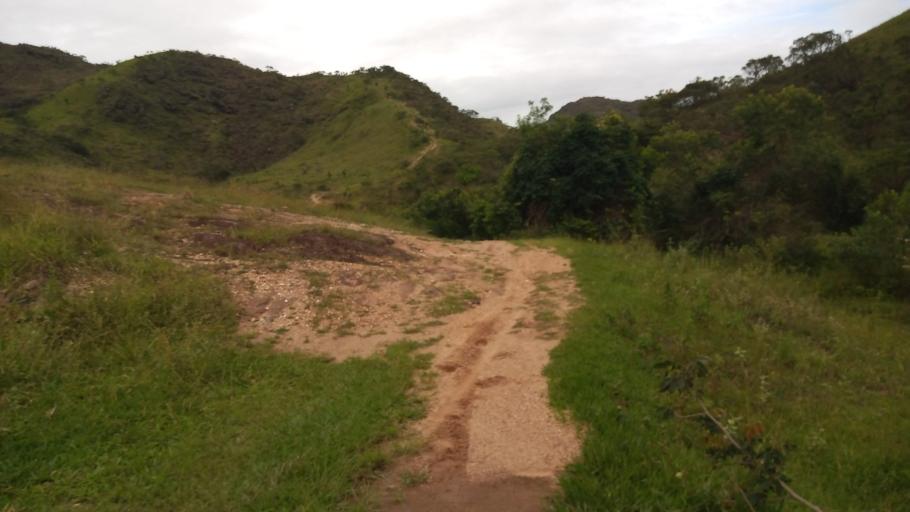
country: BR
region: Minas Gerais
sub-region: Sao Joao Del Rei
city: Sao Joao del Rei
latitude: -21.1257
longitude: -44.2707
